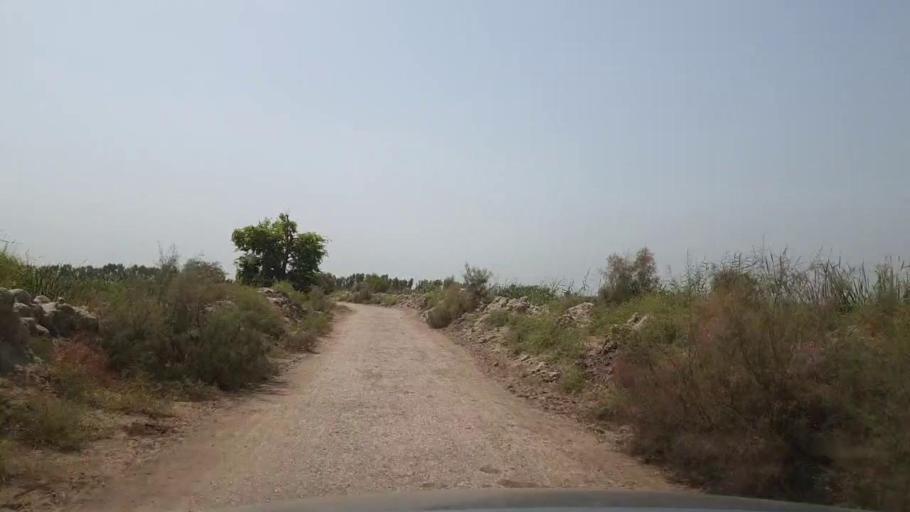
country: PK
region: Sindh
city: Garhi Yasin
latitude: 27.8895
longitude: 68.4583
